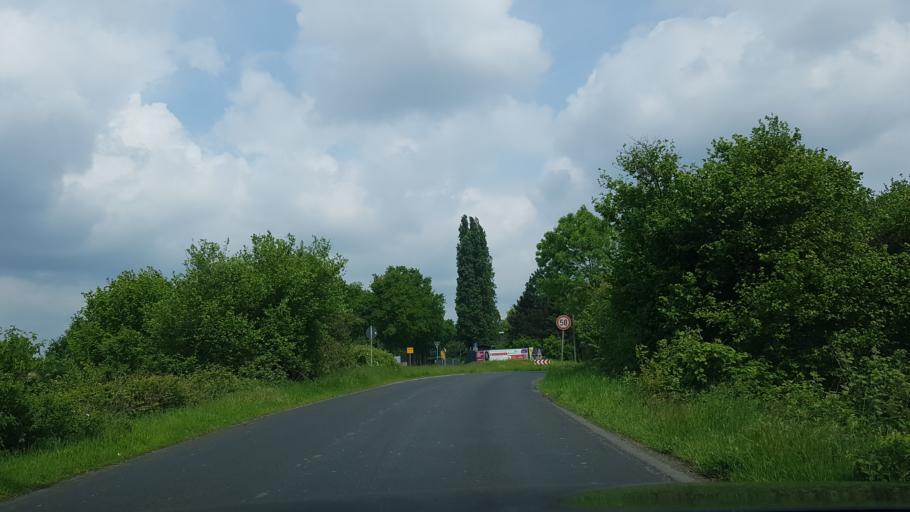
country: DE
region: North Rhine-Westphalia
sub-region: Regierungsbezirk Dusseldorf
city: Moers
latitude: 51.4240
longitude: 6.6661
